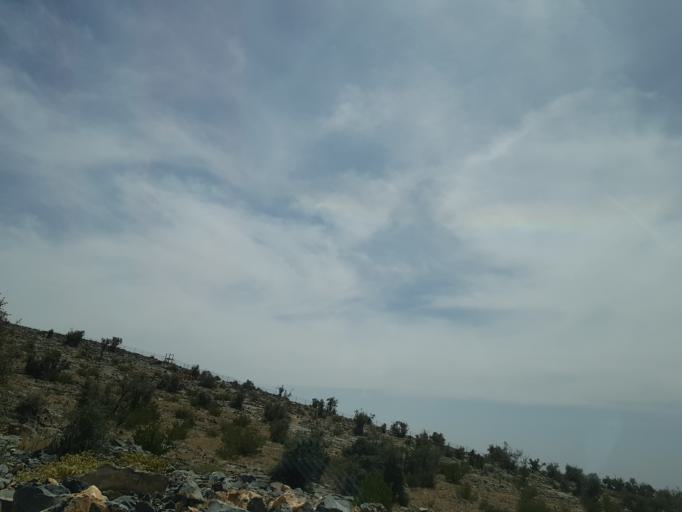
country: OM
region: Al Batinah
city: Bayt al `Awabi
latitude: 23.1418
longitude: 57.5361
